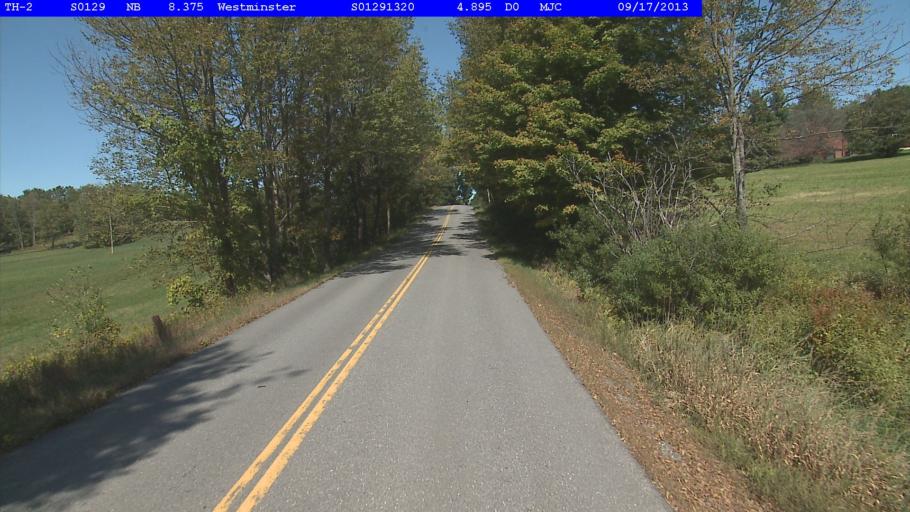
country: US
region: Vermont
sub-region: Windham County
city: Bellows Falls
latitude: 43.0855
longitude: -72.5356
